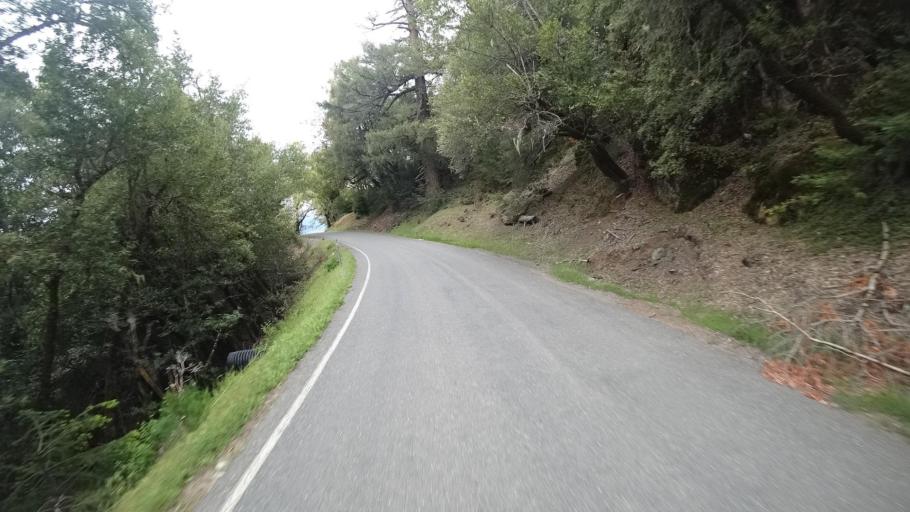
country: US
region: California
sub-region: Humboldt County
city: Redway
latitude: 40.1546
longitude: -123.5560
